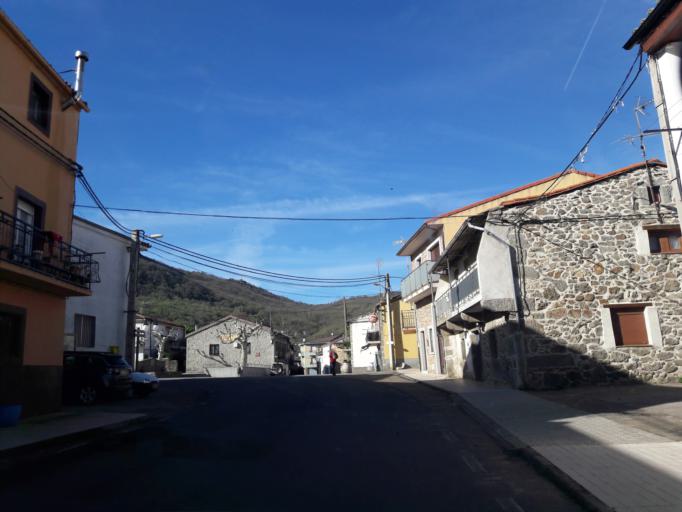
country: ES
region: Castille and Leon
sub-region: Provincia de Salamanca
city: Sanchotello
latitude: 40.4387
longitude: -5.7523
